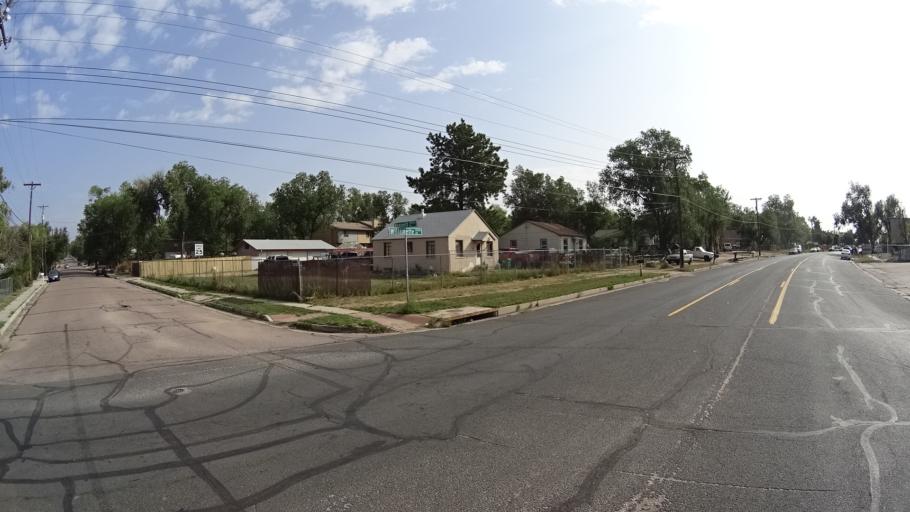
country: US
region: Colorado
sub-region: El Paso County
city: Colorado Springs
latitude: 38.8409
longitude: -104.7805
